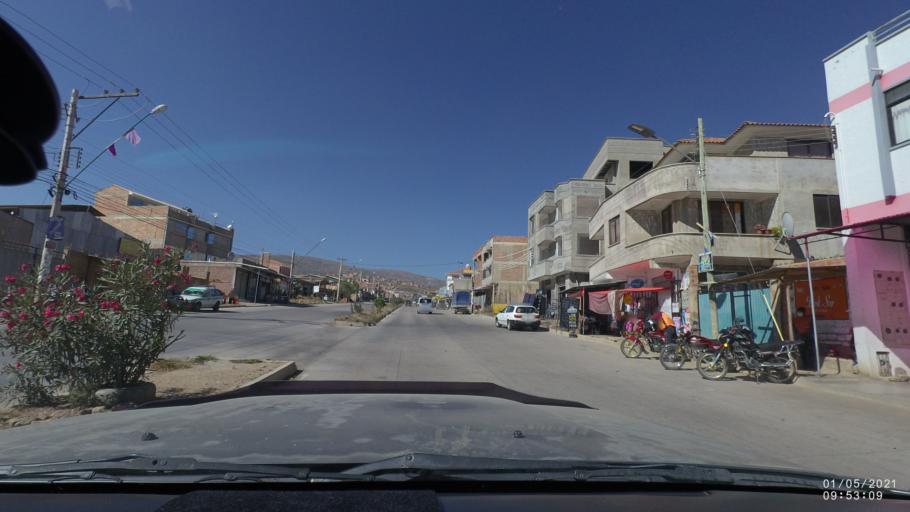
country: BO
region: Cochabamba
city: Cochabamba
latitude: -17.4833
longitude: -66.1732
